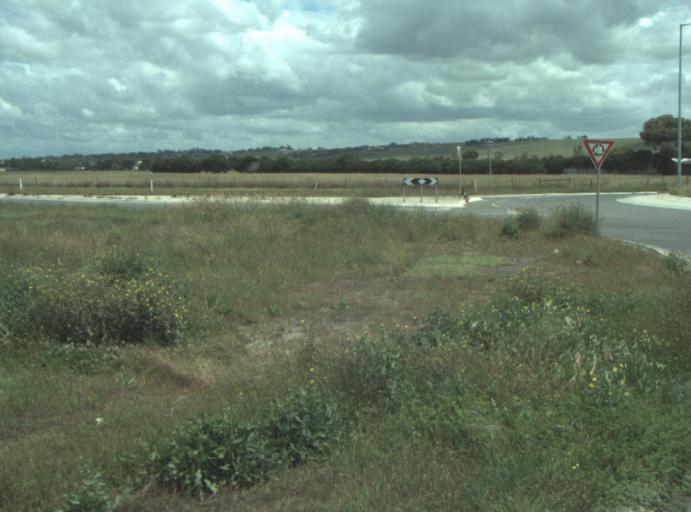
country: AU
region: Victoria
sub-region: Greater Geelong
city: Lara
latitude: -38.0481
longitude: 144.3584
